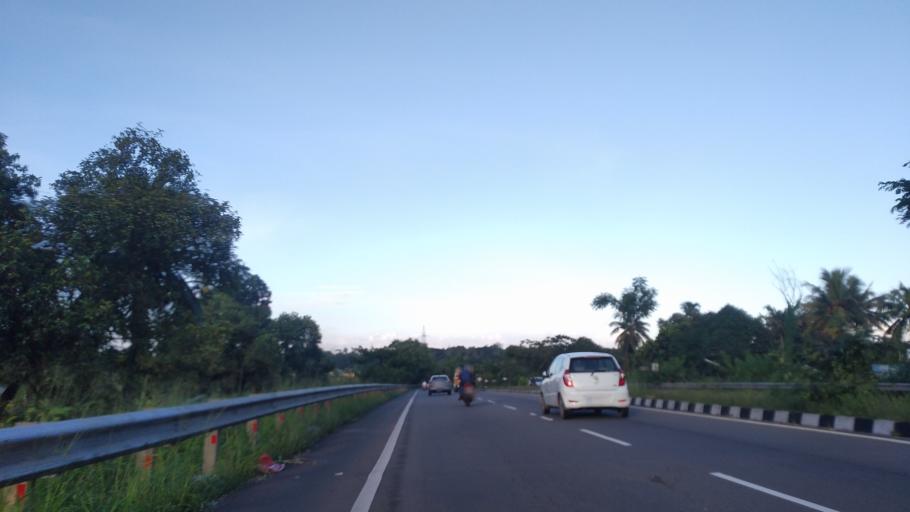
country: IN
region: Kerala
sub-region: Ernakulam
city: Elur
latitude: 10.0673
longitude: 76.2993
